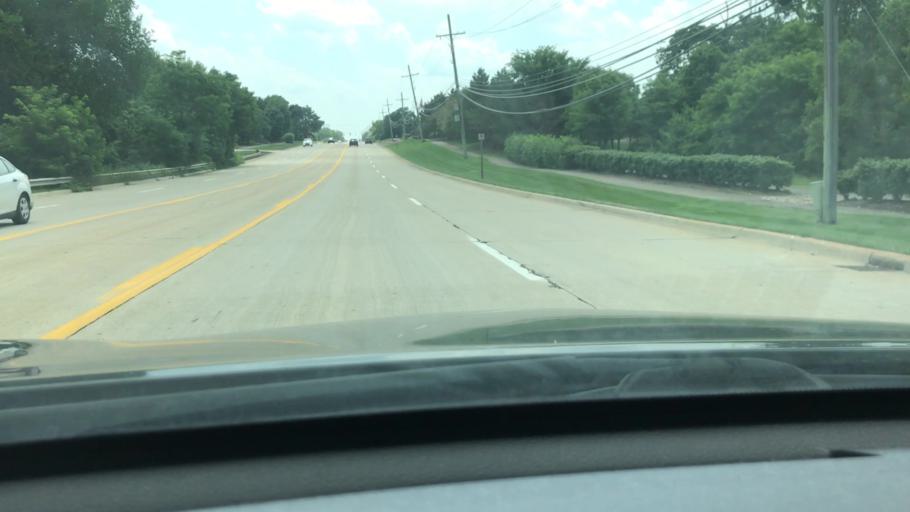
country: US
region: Michigan
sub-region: Wayne County
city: Northville
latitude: 42.4011
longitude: -83.4819
